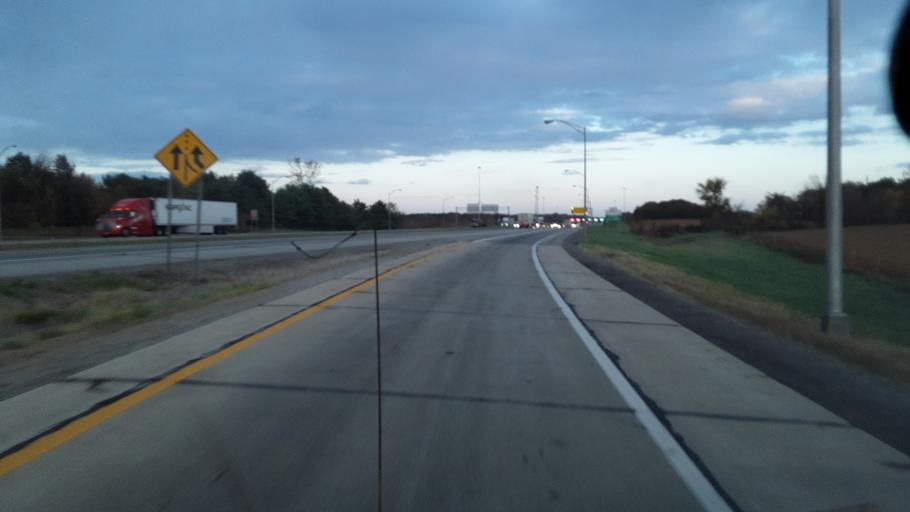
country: US
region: Ohio
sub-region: Williams County
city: Montpelier
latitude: 41.6294
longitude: -84.7632
